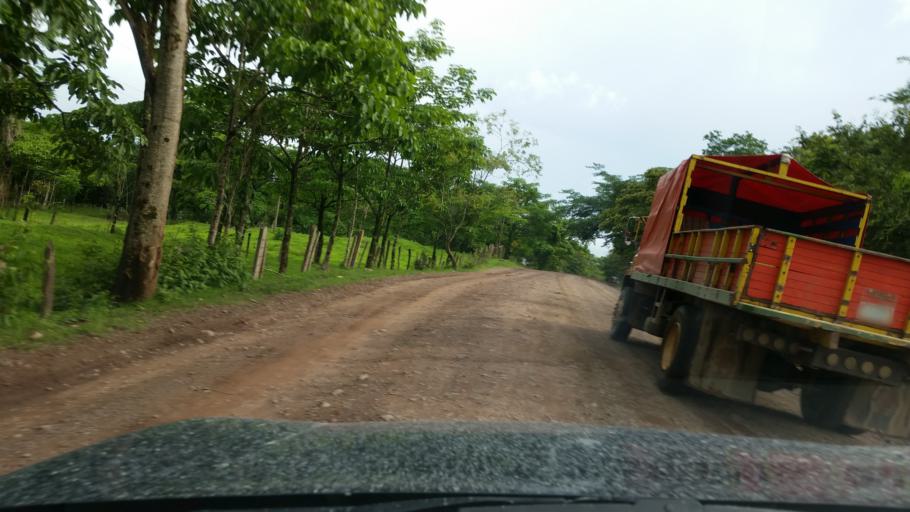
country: NI
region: Atlantico Norte (RAAN)
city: Siuna
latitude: 13.4723
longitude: -84.8441
